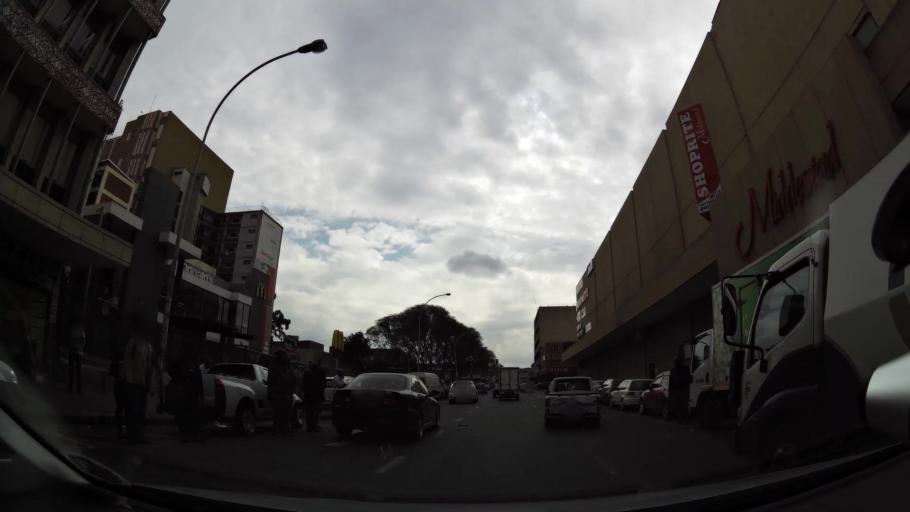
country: ZA
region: Orange Free State
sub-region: Mangaung Metropolitan Municipality
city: Bloemfontein
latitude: -29.1166
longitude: 26.2207
